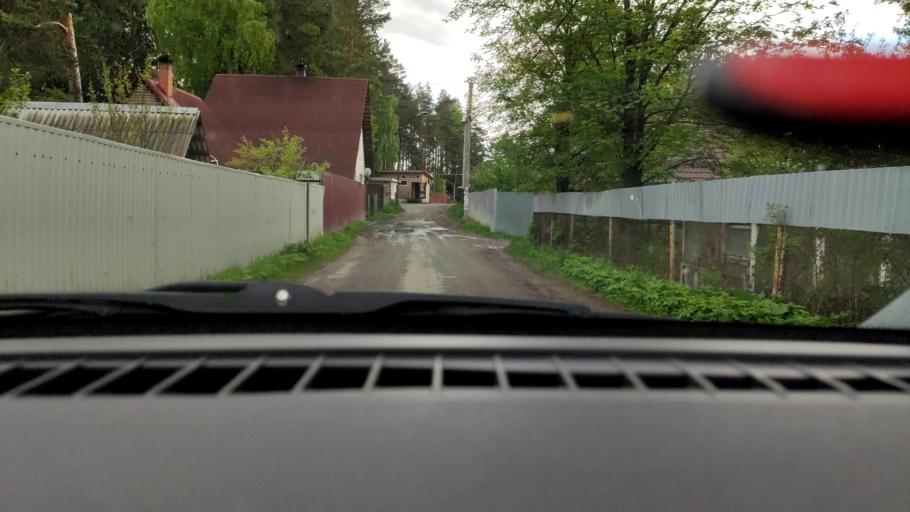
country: RU
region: Perm
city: Kondratovo
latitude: 58.0564
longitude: 56.1325
